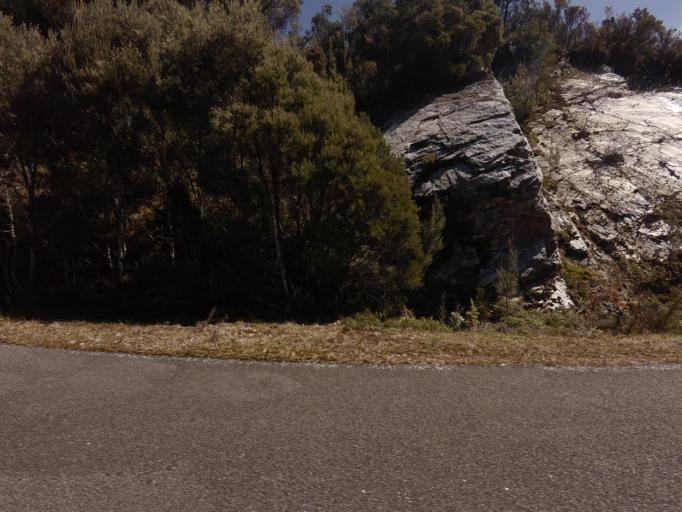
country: AU
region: Tasmania
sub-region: West Coast
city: Queenstown
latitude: -42.7535
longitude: 145.9835
